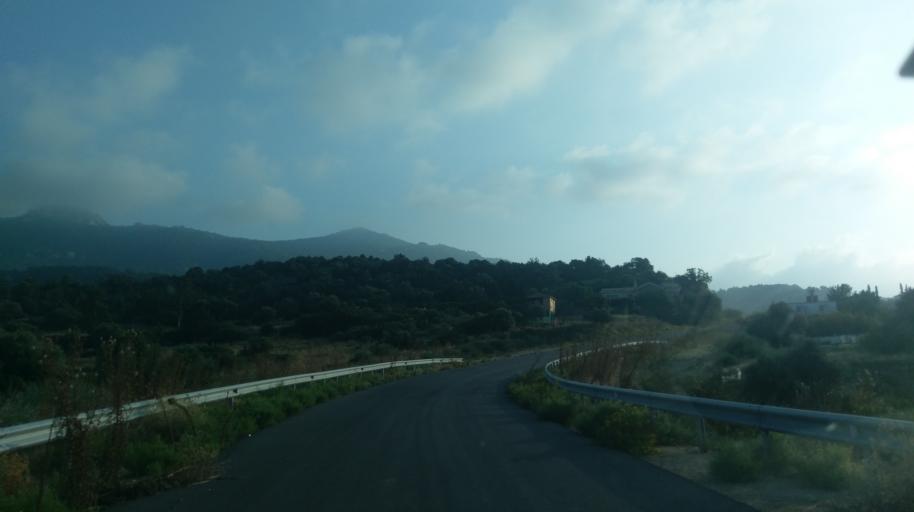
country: CY
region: Ammochostos
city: Trikomo
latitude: 35.4240
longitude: 33.9087
